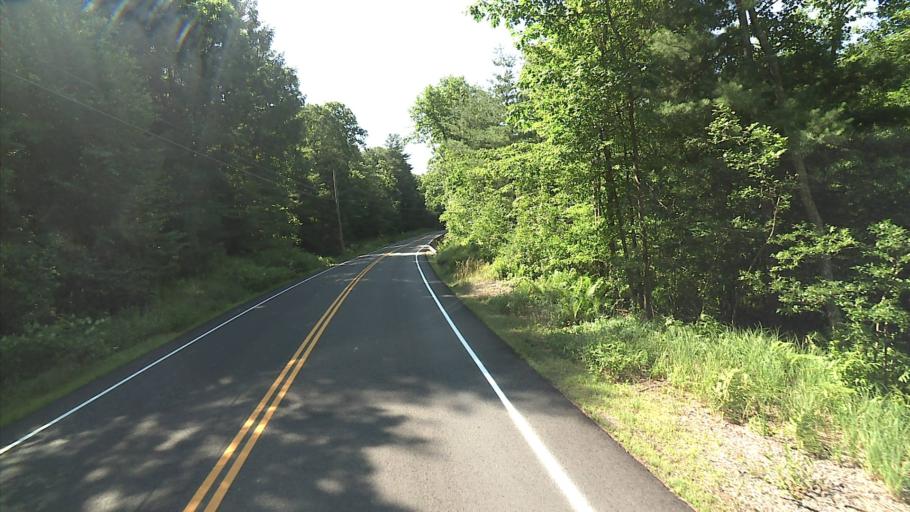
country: US
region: Connecticut
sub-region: Litchfield County
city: Terryville
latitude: 41.7355
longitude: -73.0158
